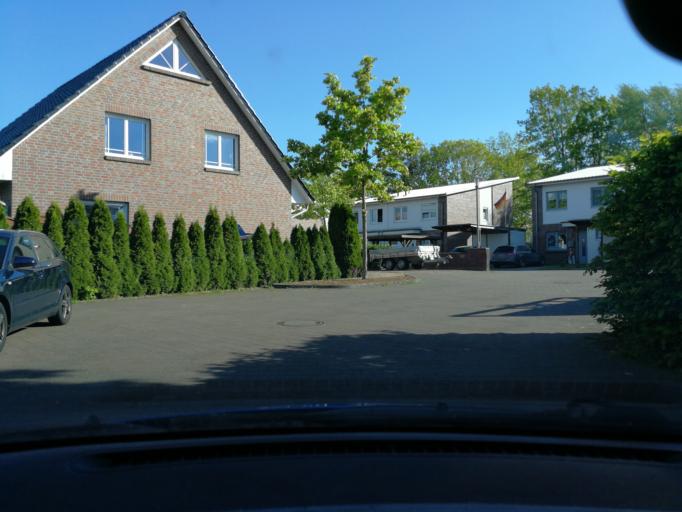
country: DE
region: Lower Saxony
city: Winsen
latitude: 53.3647
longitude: 10.1931
